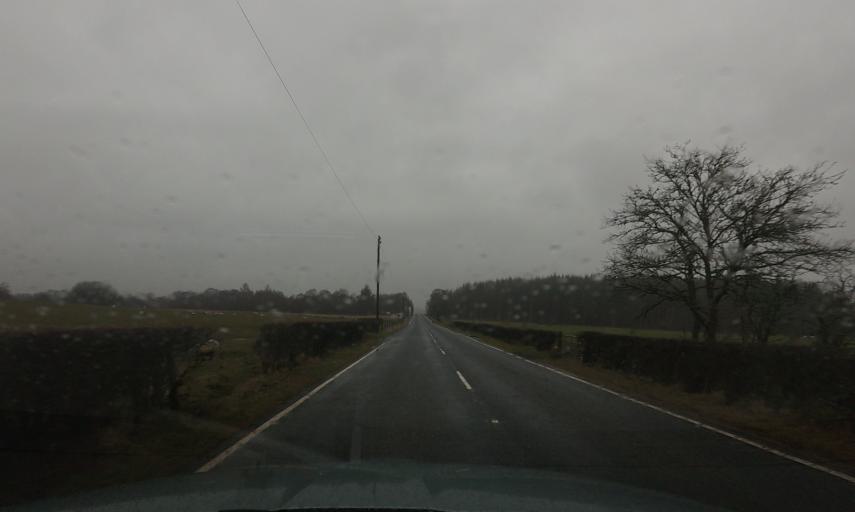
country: GB
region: Scotland
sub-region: Stirling
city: Balfron
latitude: 56.1170
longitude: -4.3590
